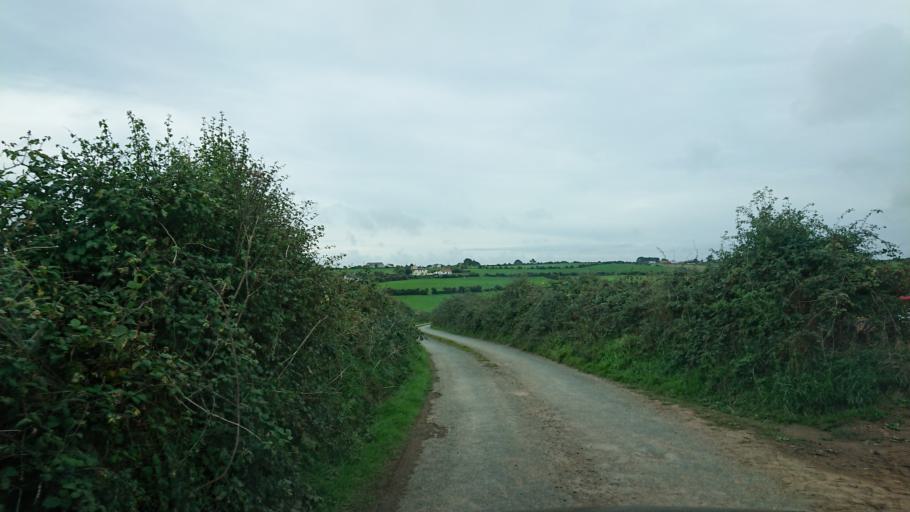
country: IE
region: Munster
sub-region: Waterford
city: Dunmore East
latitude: 52.1745
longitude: -6.9948
